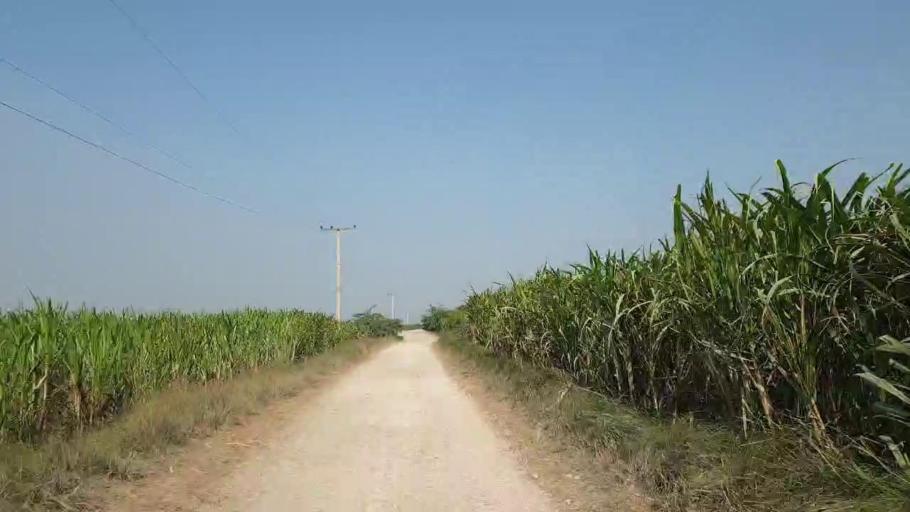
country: PK
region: Sindh
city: Bulri
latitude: 24.9353
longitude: 68.3841
